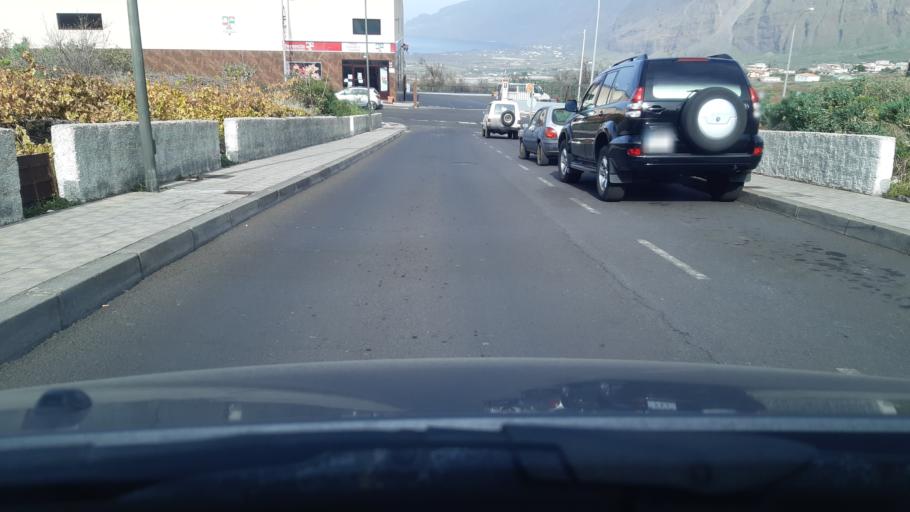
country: ES
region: Canary Islands
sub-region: Provincia de Santa Cruz de Tenerife
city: Frontera
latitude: 27.7529
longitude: -18.0154
